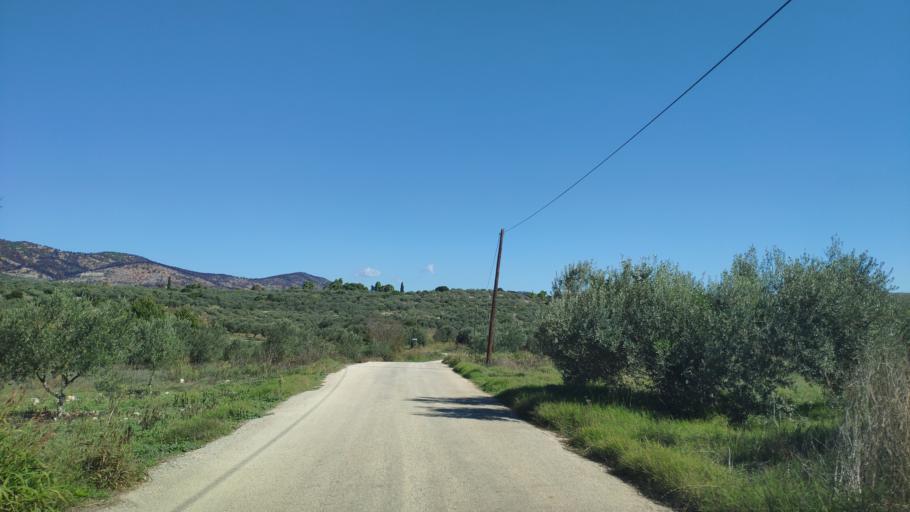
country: GR
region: Peloponnese
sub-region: Nomos Korinthias
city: Athikia
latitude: 37.8365
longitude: 22.9159
